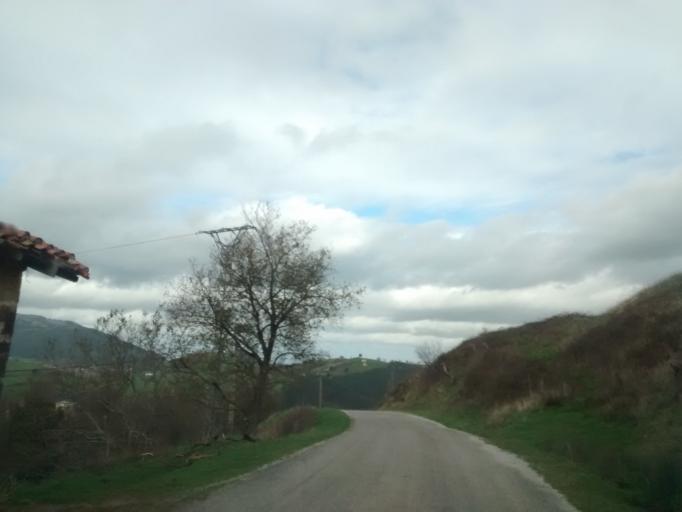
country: ES
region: Cantabria
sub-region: Provincia de Cantabria
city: Lierganes
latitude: 43.3354
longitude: -3.7384
